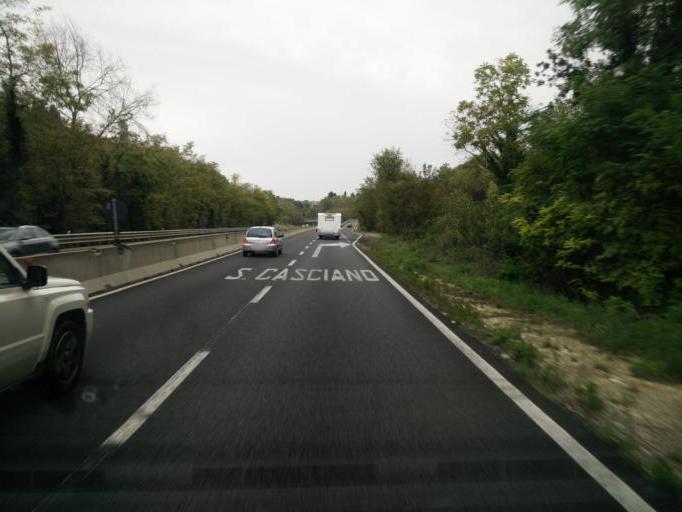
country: IT
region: Tuscany
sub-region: Province of Florence
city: San Casciano in Val di Pesa
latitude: 43.6495
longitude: 11.1856
